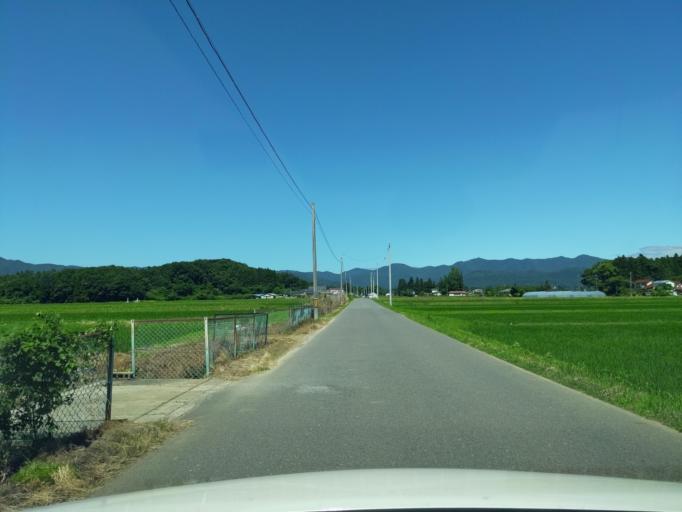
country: JP
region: Fukushima
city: Koriyama
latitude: 37.3856
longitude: 140.2933
